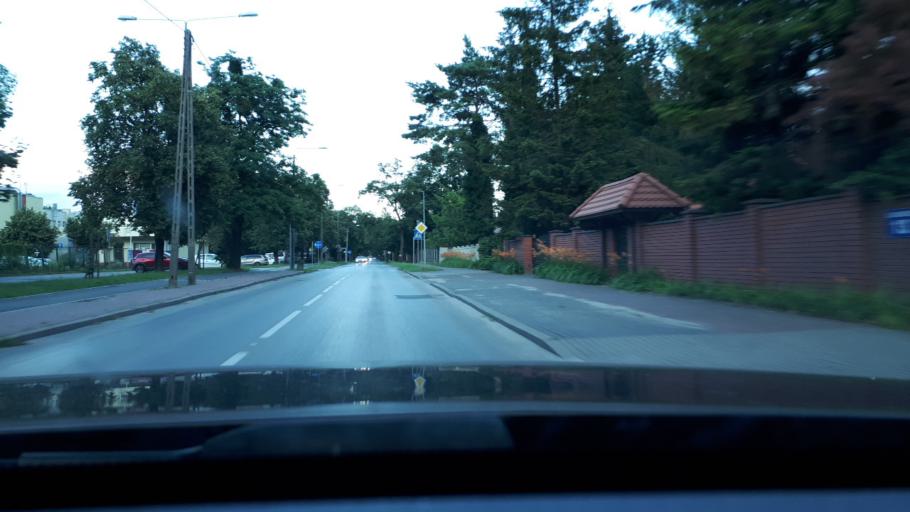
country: PL
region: Masovian Voivodeship
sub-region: Powiat pruszkowski
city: Komorow
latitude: 52.1588
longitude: 20.8191
